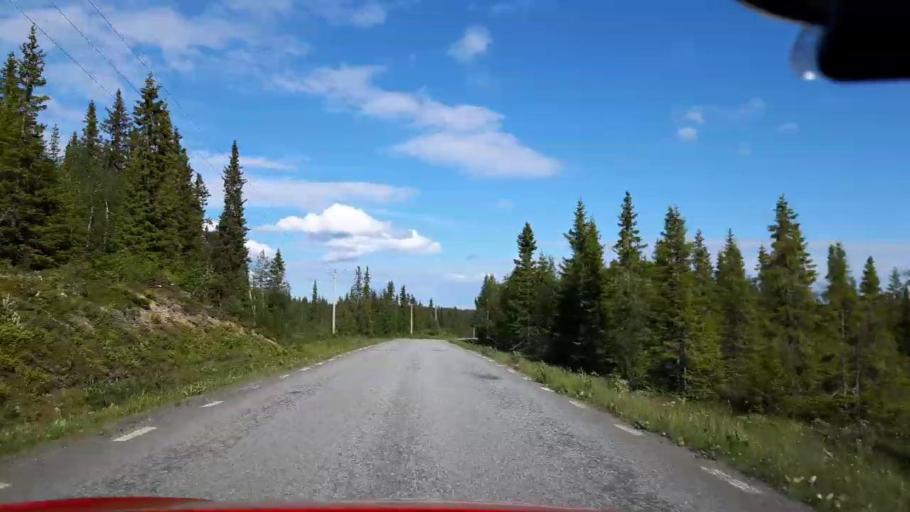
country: SE
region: Jaemtland
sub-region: Krokoms Kommun
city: Valla
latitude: 63.6957
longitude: 14.1920
